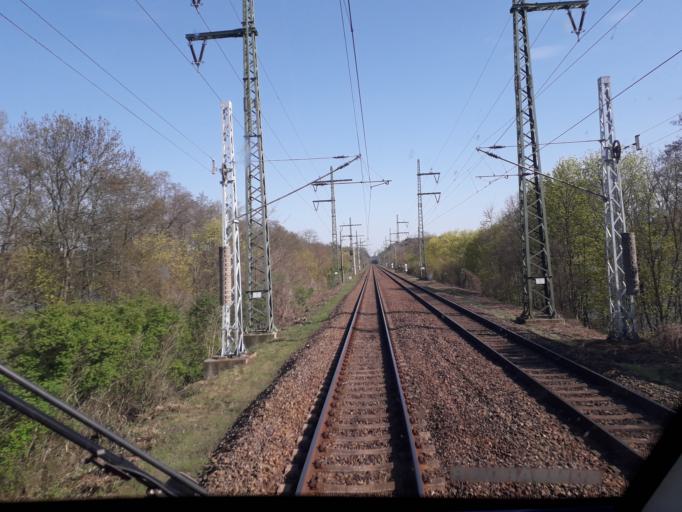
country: DE
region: Brandenburg
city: Potsdam
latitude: 52.3685
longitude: 13.0196
